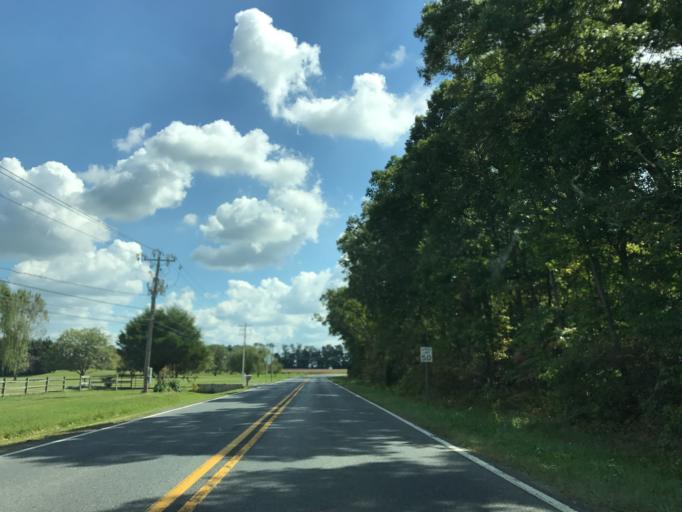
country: US
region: Maryland
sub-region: Queen Anne's County
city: Centreville
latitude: 39.0264
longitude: -76.0217
